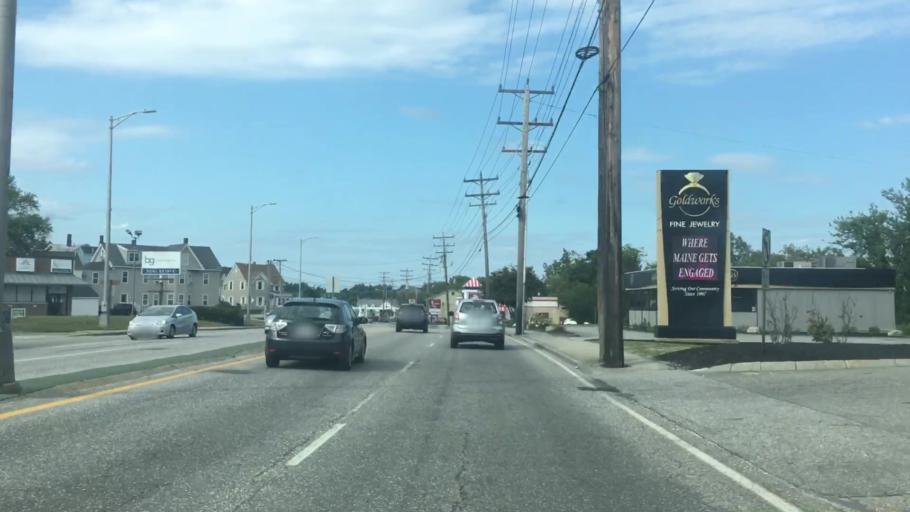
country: US
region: Maine
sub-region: Androscoggin County
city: Auburn
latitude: 44.1028
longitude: -70.2261
